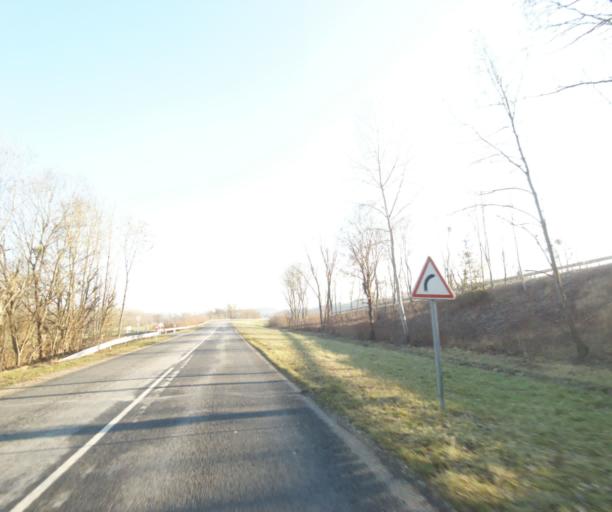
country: FR
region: Champagne-Ardenne
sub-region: Departement de la Haute-Marne
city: Bienville
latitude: 48.5688
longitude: 5.0396
